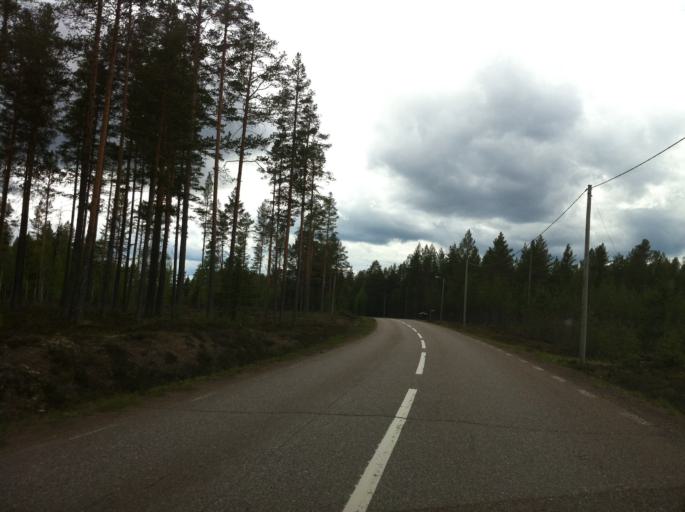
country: NO
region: Hedmark
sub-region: Trysil
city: Innbygda
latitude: 61.4297
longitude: 13.0913
